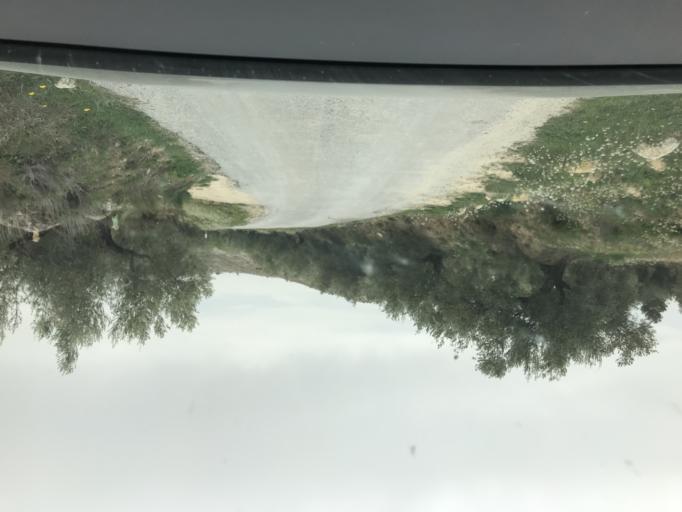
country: ES
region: Andalusia
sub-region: Provincia de Granada
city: Castril
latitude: 37.8237
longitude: -2.7703
